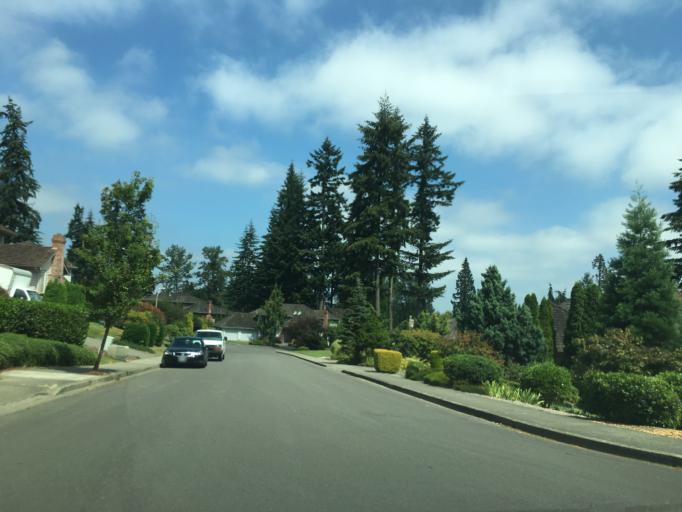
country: US
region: Washington
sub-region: King County
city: Woodinville
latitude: 47.7469
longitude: -122.1799
